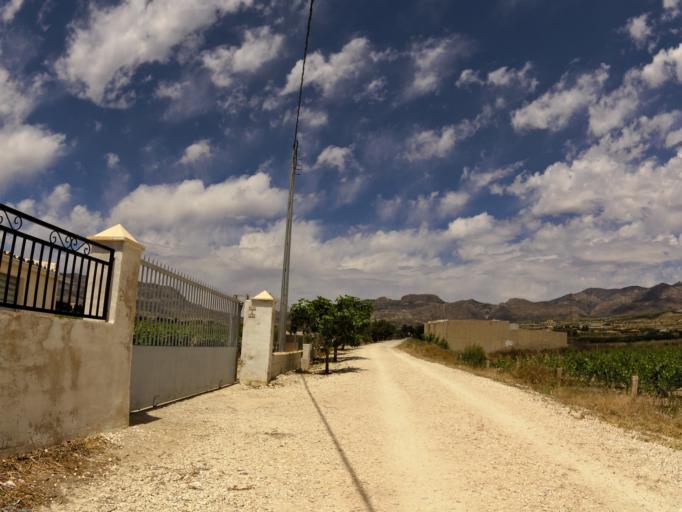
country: ES
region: Valencia
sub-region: Provincia de Alicante
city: Agost
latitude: 38.4394
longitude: -0.6493
